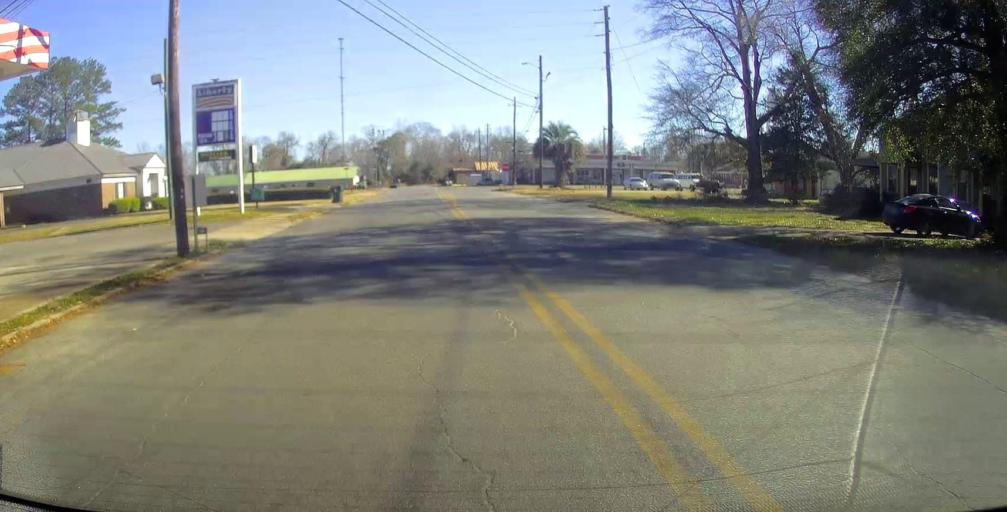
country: US
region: Georgia
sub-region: Macon County
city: Oglethorpe
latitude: 32.2951
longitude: -84.0602
